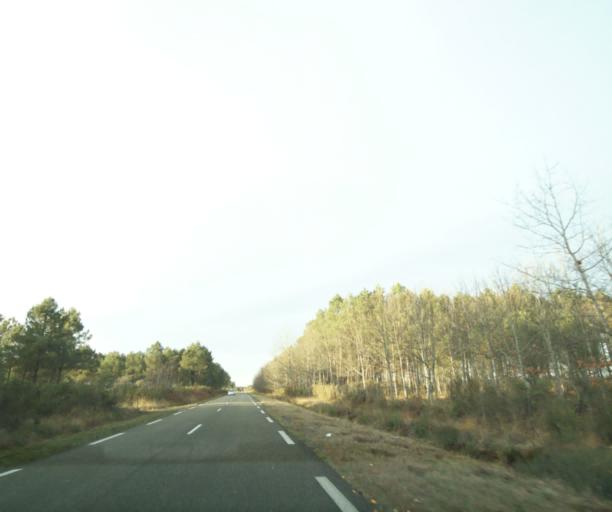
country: FR
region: Aquitaine
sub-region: Departement des Landes
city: Gabarret
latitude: 44.1447
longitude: -0.1236
